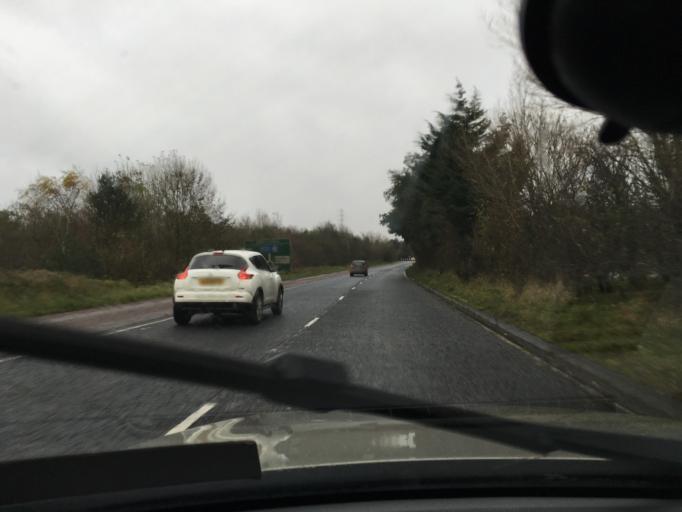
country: GB
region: Northern Ireland
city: Carnmoney
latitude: 54.6951
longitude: -5.9697
